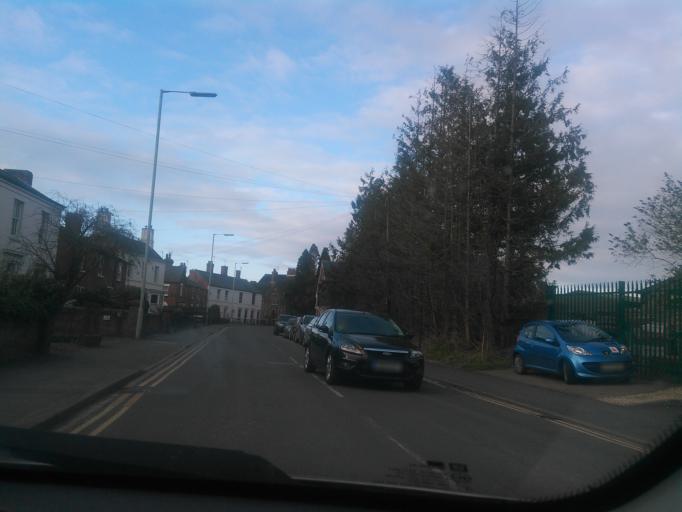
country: GB
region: England
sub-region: Telford and Wrekin
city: Newport
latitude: 52.7652
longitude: -2.3788
